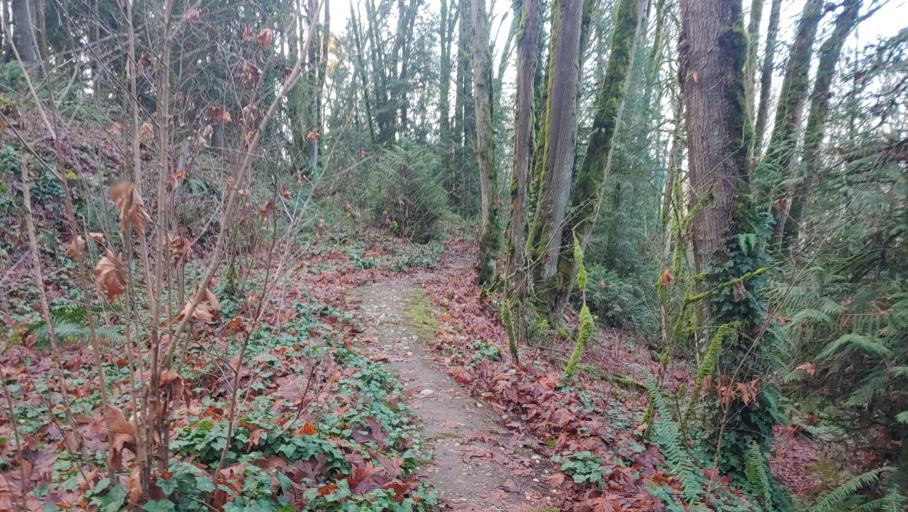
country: US
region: Washington
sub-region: King County
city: Eastgate
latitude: 47.5692
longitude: -122.1502
